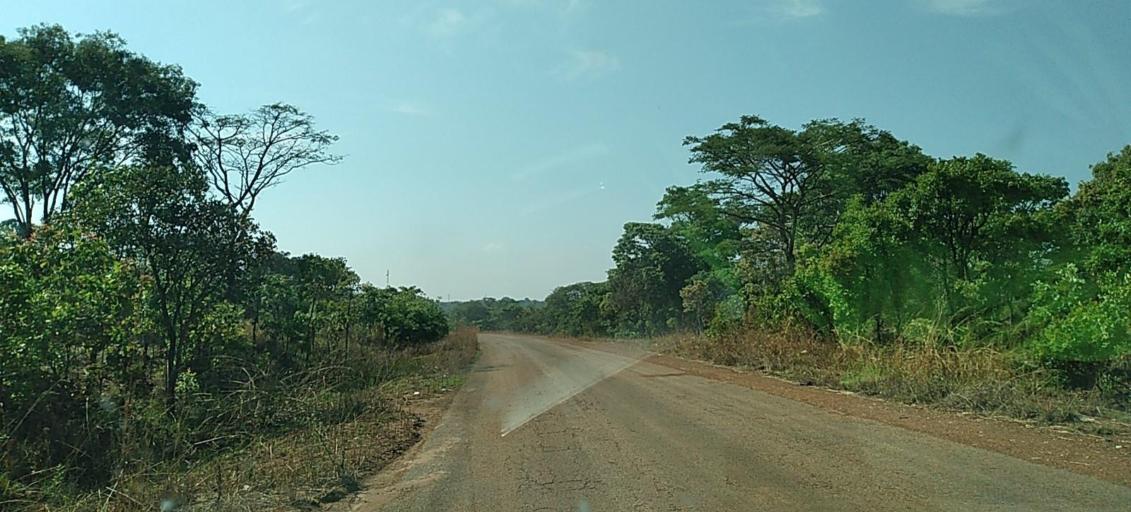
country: ZM
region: North-Western
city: Mwinilunga
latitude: -11.8018
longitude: 25.0765
